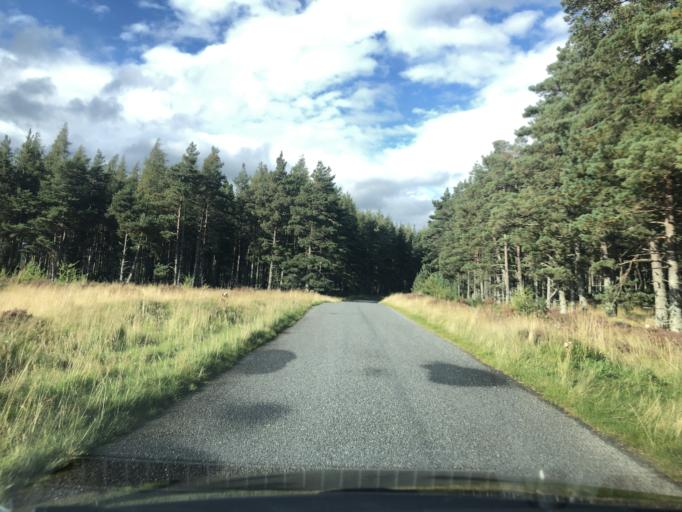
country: GB
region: Scotland
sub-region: Highland
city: Aviemore
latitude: 57.0964
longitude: -3.8926
